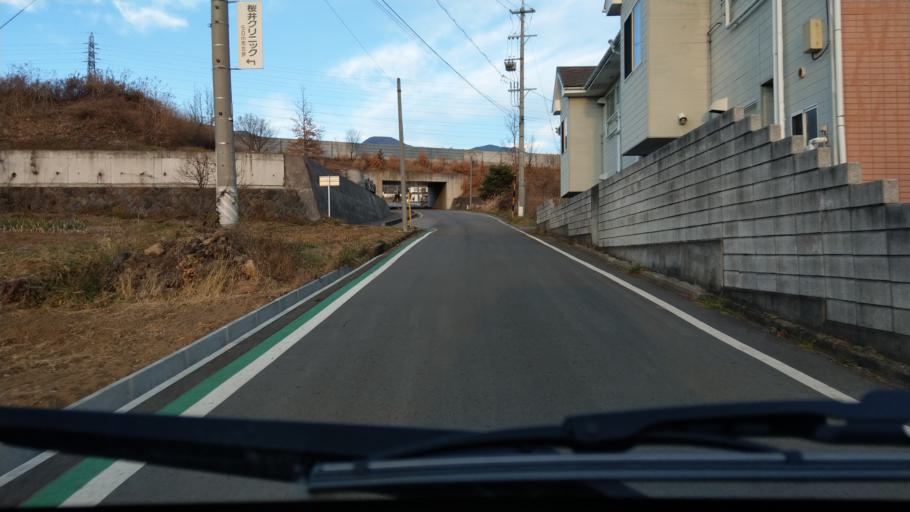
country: JP
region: Nagano
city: Komoro
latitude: 36.3472
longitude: 138.3929
